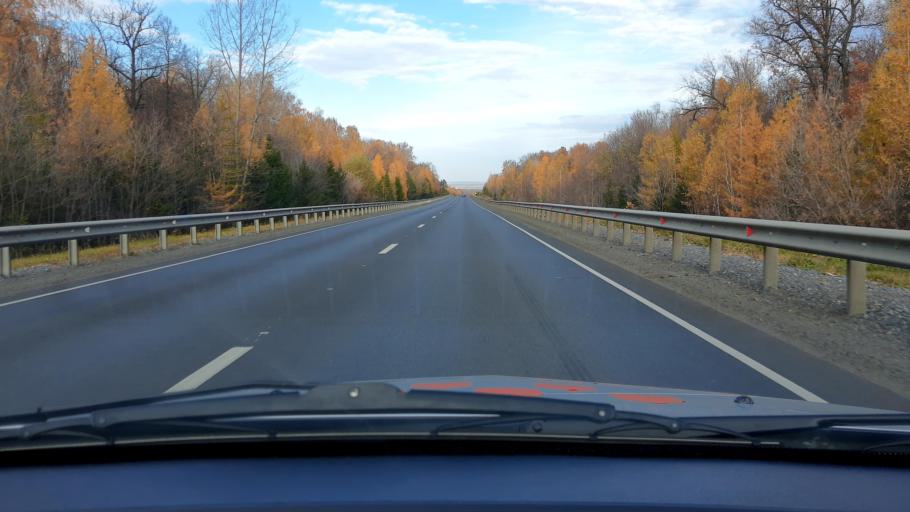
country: RU
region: Bashkortostan
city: Avdon
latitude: 54.8389
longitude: 55.7176
